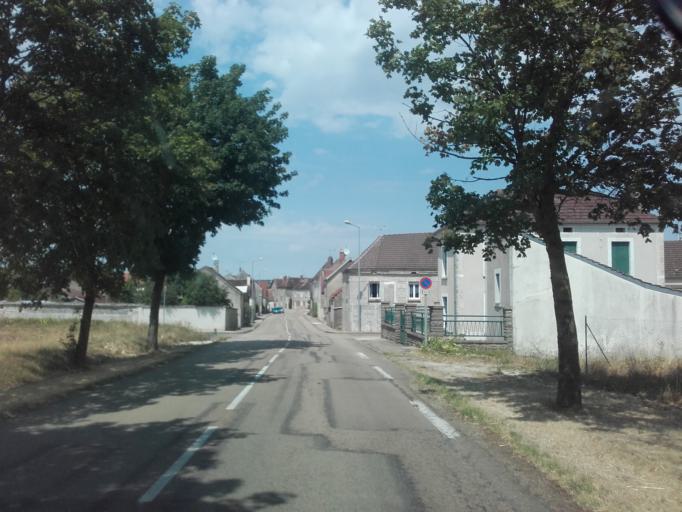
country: FR
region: Bourgogne
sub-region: Departement de l'Yonne
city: Chablis
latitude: 47.7263
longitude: 3.8534
